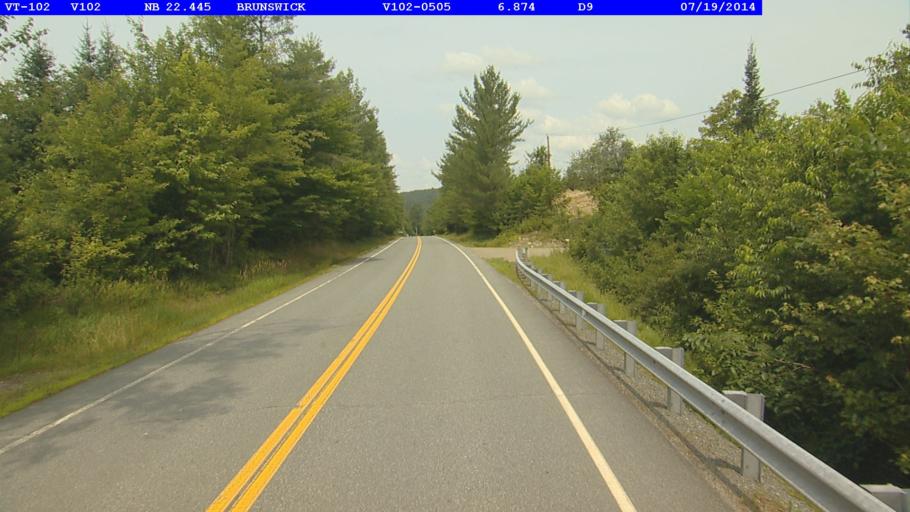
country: US
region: New Hampshire
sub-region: Coos County
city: Stratford
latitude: 44.7463
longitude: -71.6316
